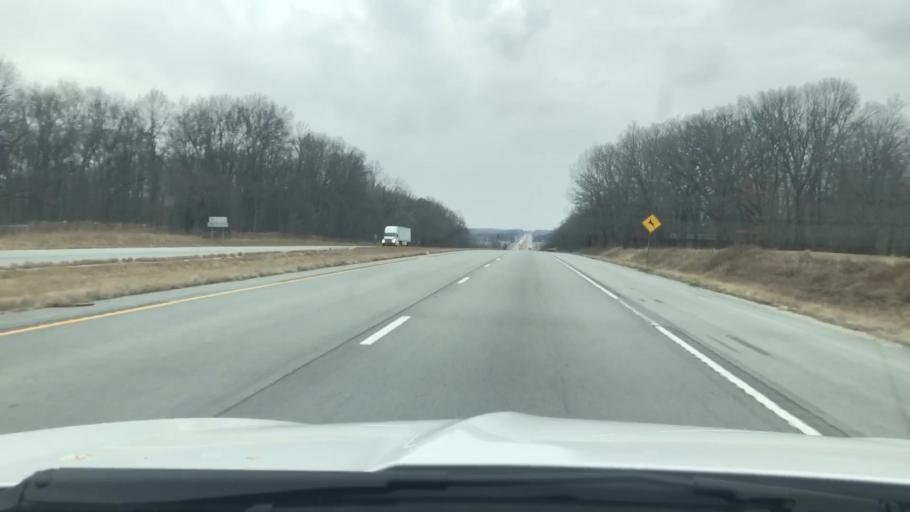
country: US
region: Indiana
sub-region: Miami County
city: Peru
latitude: 40.7936
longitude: -86.1290
